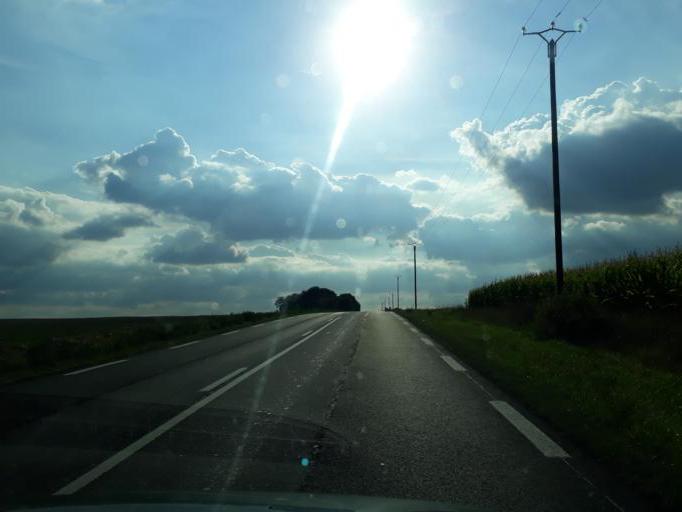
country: FR
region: Centre
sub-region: Departement du Loir-et-Cher
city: La Ville-aux-Clercs
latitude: 47.8927
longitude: 1.1024
